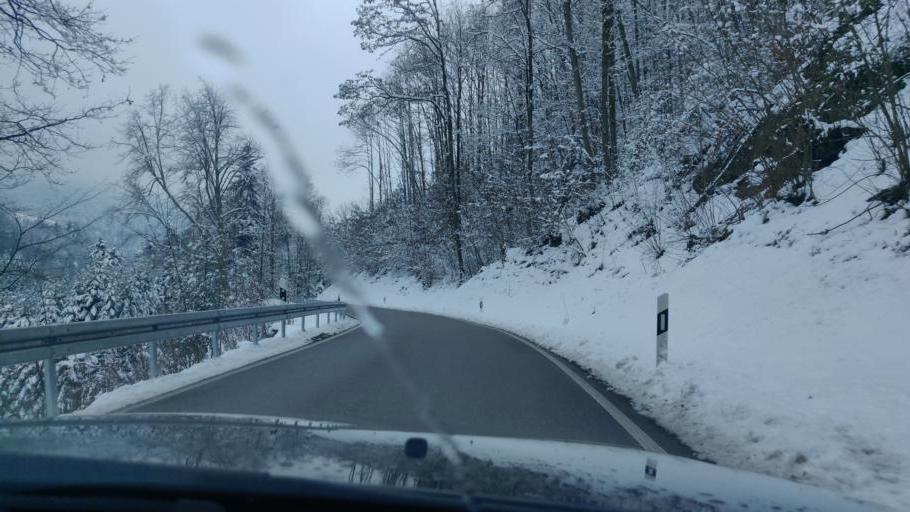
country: DE
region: Baden-Wuerttemberg
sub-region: Freiburg Region
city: Haslach
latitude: 48.5662
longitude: 8.0900
